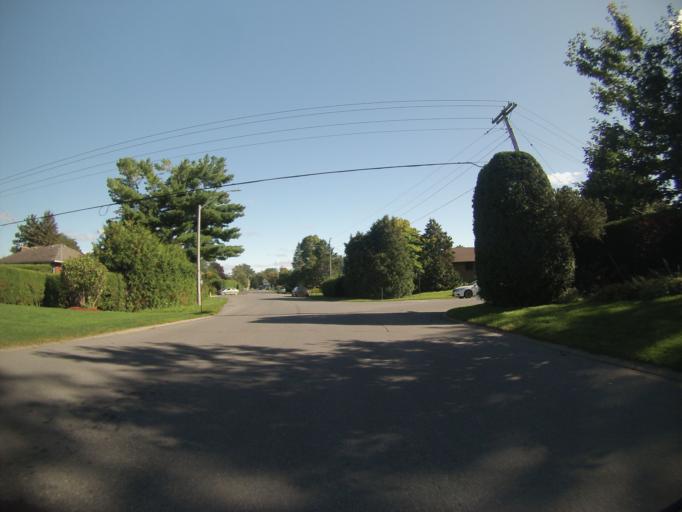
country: CA
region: Ontario
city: Ottawa
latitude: 45.3465
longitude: -75.7507
